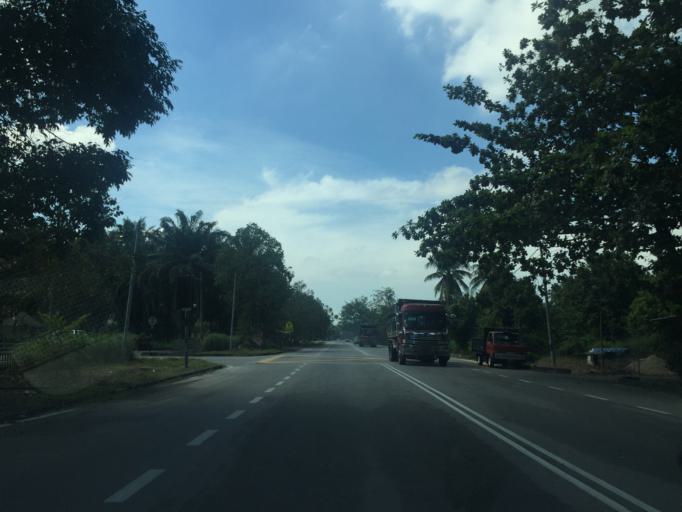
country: MY
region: Penang
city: Tasek Glugor
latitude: 5.5007
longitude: 100.5221
